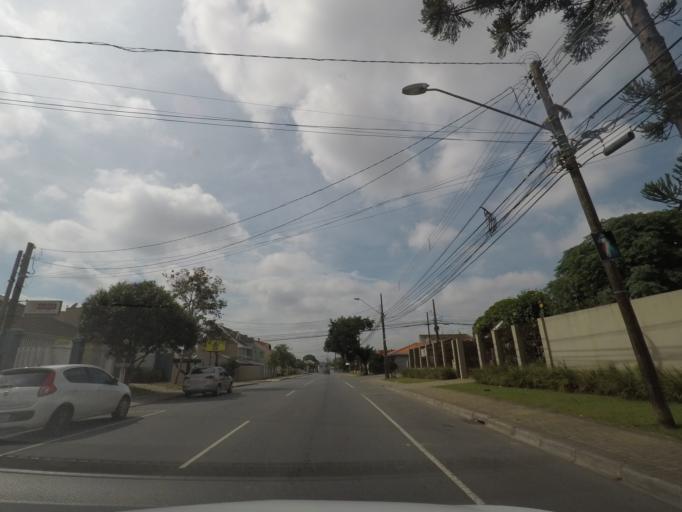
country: BR
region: Parana
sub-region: Curitiba
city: Curitiba
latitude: -25.4796
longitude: -49.3086
